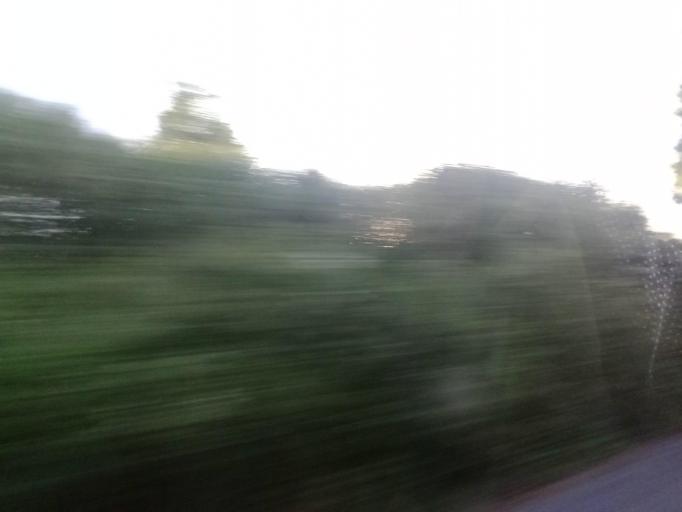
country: IE
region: Leinster
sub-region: Kilkenny
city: Castlecomer
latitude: 52.7446
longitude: -7.2356
